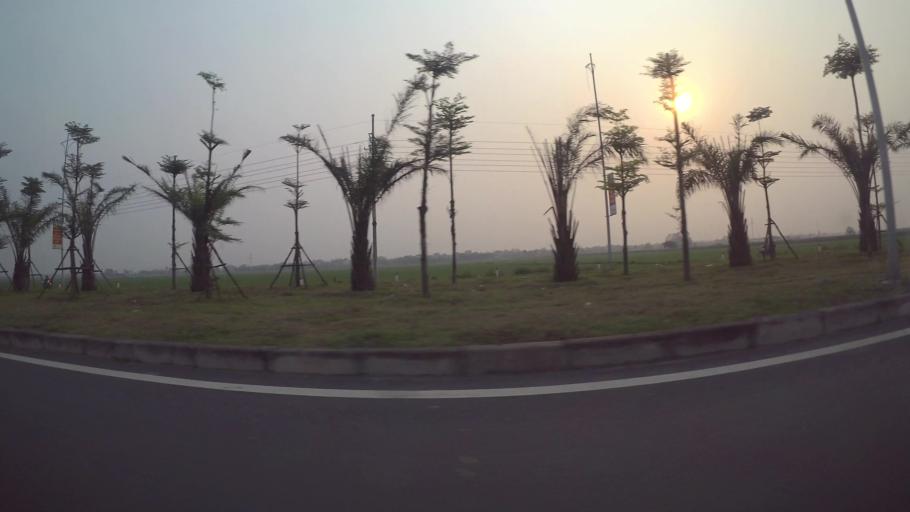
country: VN
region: Ha Noi
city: Kim Bai
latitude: 20.8898
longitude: 105.7954
